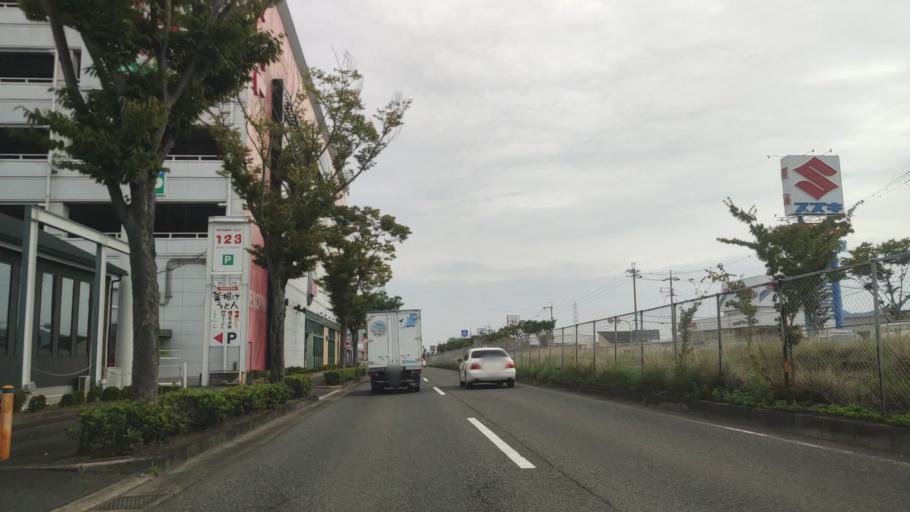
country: JP
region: Osaka
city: Tondabayashicho
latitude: 34.4454
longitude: 135.5540
